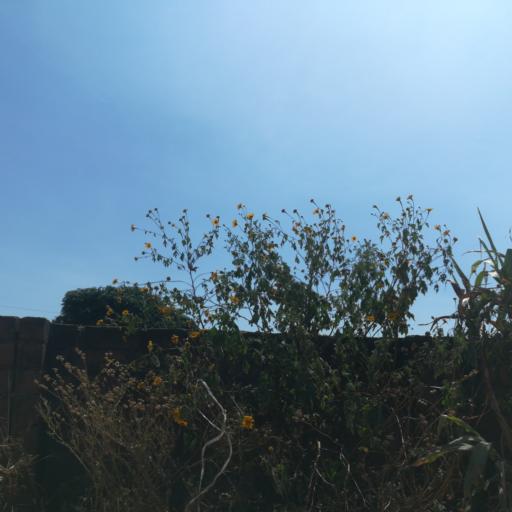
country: NG
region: Plateau
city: Bukuru
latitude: 9.8423
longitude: 8.9089
